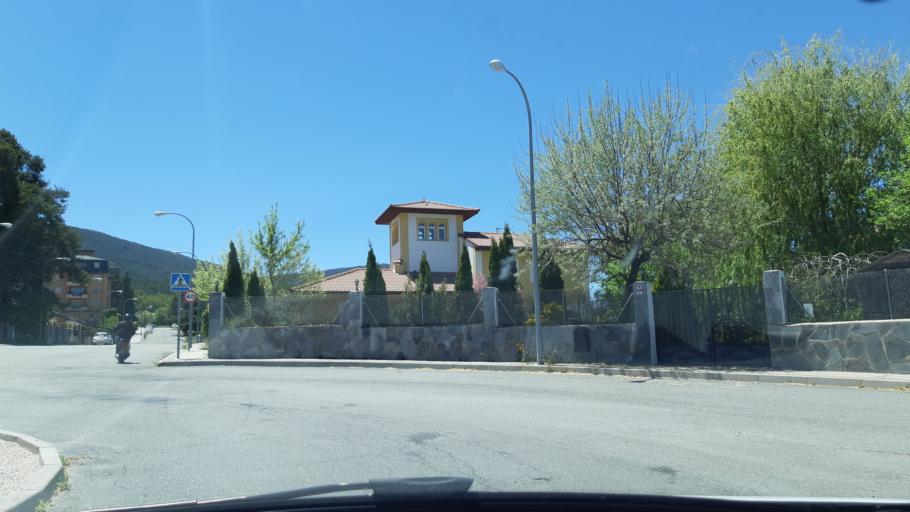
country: ES
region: Castille and Leon
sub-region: Provincia de Avila
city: Peguerinos
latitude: 40.7184
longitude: -4.1949
